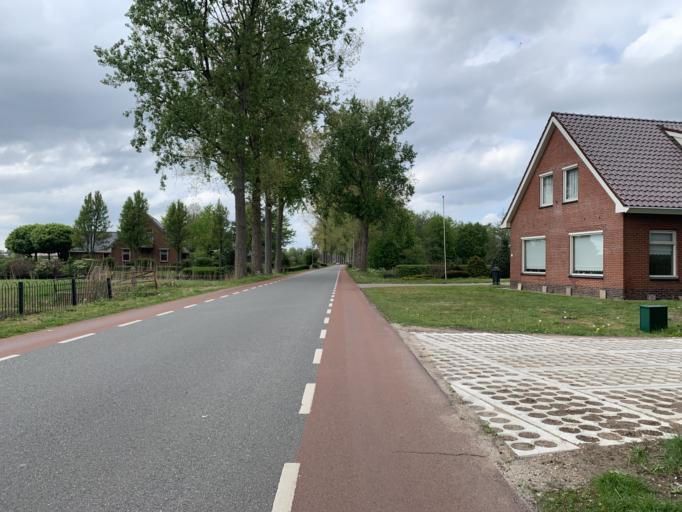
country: NL
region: Groningen
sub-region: Gemeente Haren
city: Haren
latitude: 53.2104
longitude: 6.6450
